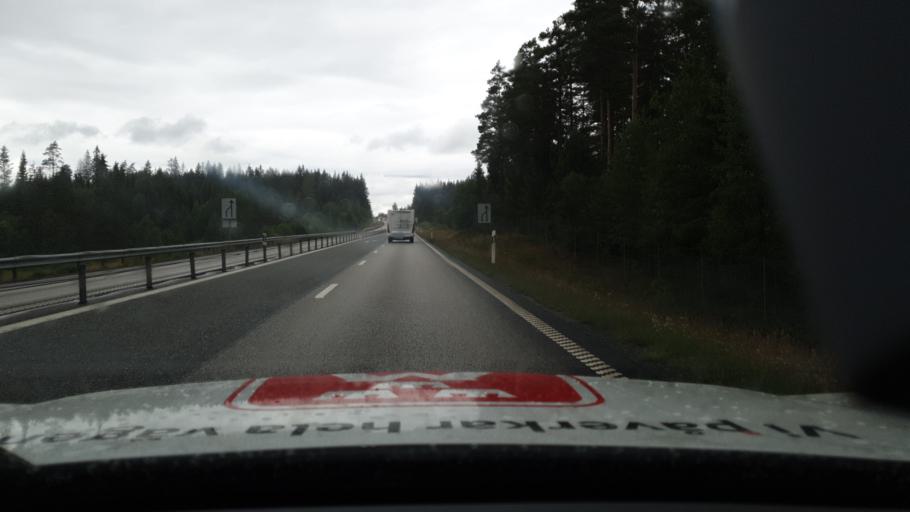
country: SE
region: Joenkoeping
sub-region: Nassjo Kommun
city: Malmback
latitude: 57.6953
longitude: 14.4457
